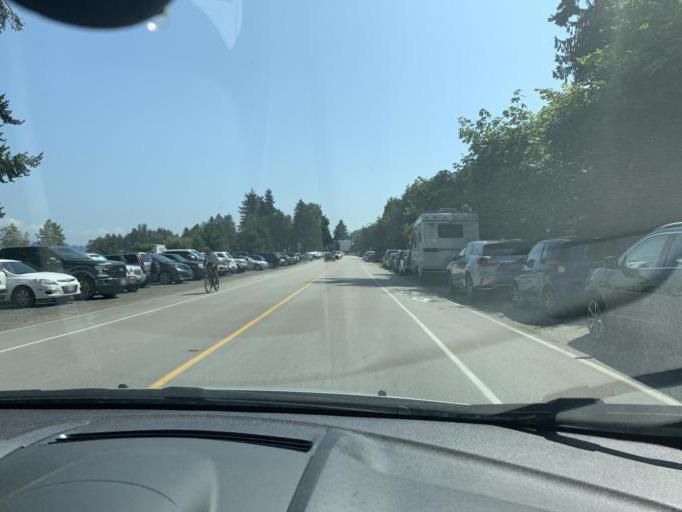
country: CA
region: British Columbia
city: West End
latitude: 49.2754
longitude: -123.2133
